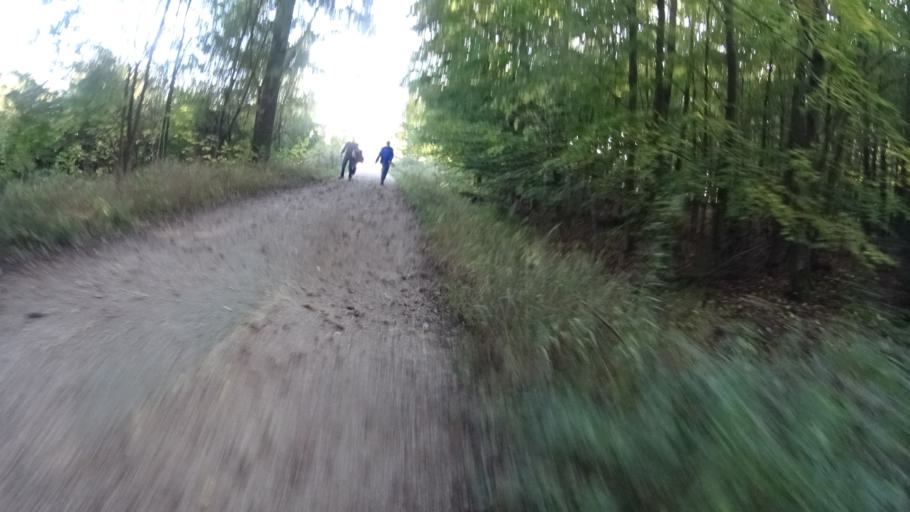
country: DE
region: Bavaria
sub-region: Upper Bavaria
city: Bohmfeld
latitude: 48.8478
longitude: 11.3609
